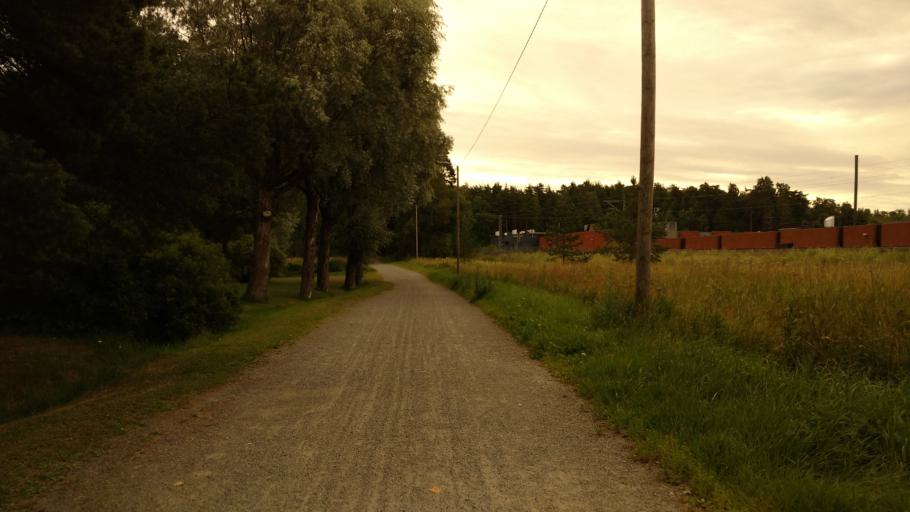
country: FI
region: Varsinais-Suomi
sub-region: Turku
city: Kaarina
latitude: 60.4395
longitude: 22.3267
